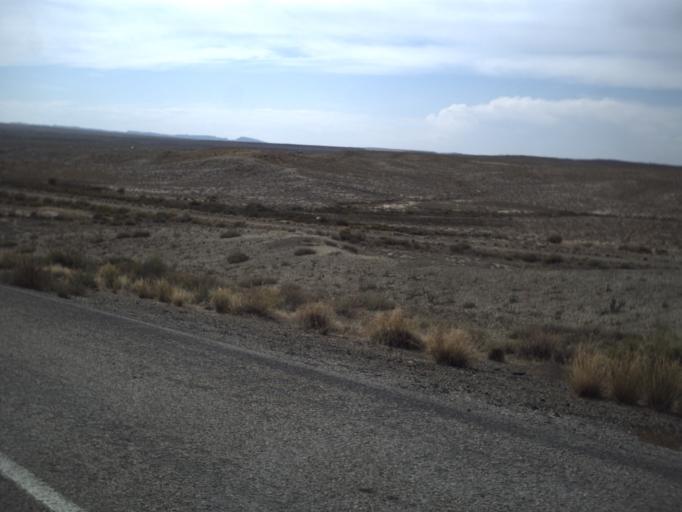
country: US
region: Utah
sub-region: Grand County
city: Moab
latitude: 38.9384
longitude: -109.4094
